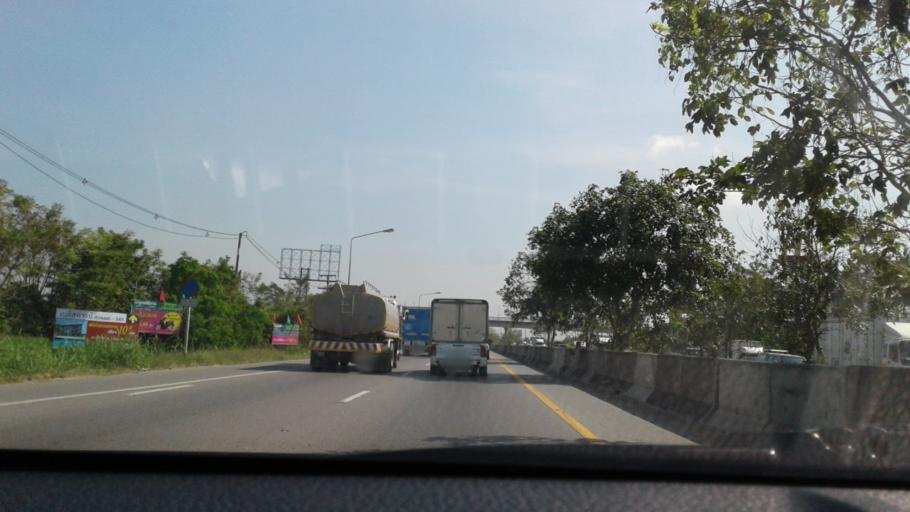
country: TH
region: Nonthaburi
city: Pak Kret
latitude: 13.9554
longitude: 100.4859
